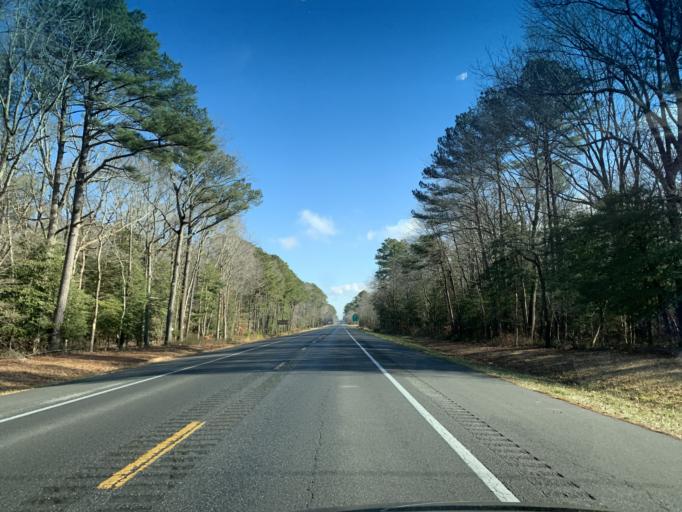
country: US
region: Maryland
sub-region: Worcester County
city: Berlin
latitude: 38.3771
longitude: -75.2327
